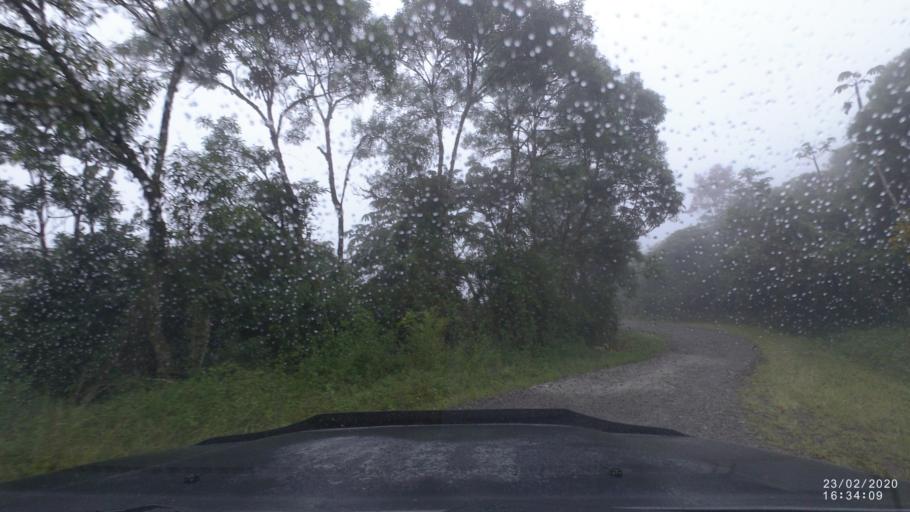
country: BO
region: Cochabamba
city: Colomi
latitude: -17.0903
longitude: -65.9965
